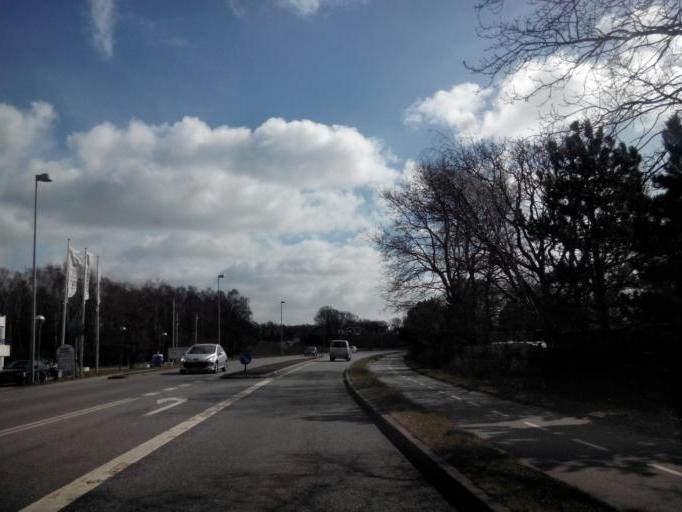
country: DK
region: Central Jutland
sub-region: Syddjurs Kommune
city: Ebeltoft
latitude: 56.2138
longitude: 10.6762
